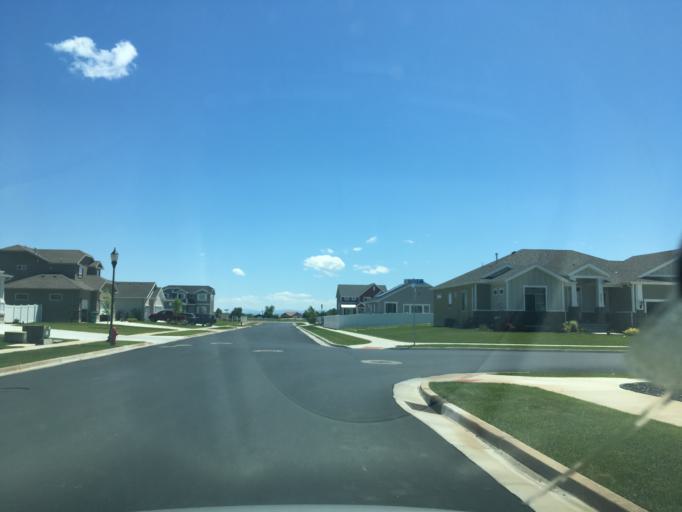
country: US
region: Utah
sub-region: Davis County
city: Layton
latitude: 41.0510
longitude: -112.0058
